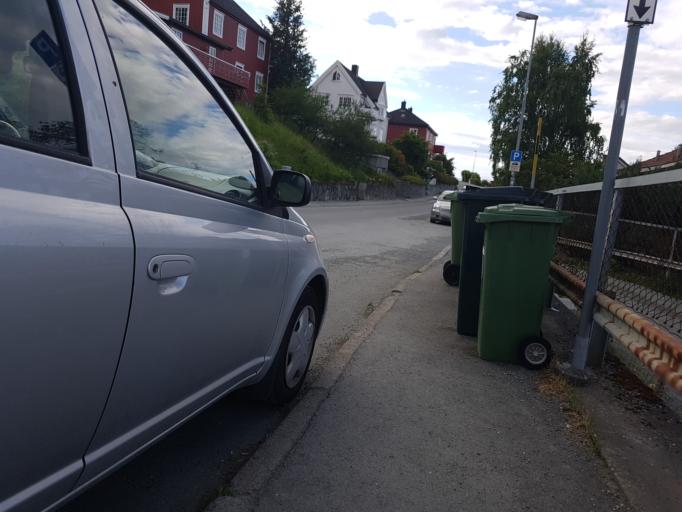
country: NO
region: Sor-Trondelag
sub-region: Trondheim
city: Trondheim
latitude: 63.4221
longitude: 10.3689
